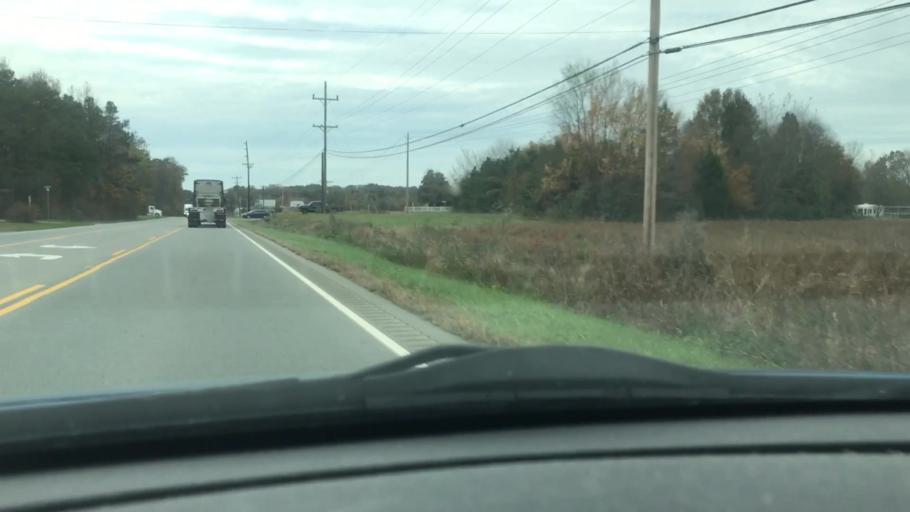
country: US
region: North Carolina
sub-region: Davidson County
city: Thomasville
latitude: 35.7886
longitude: -80.1360
